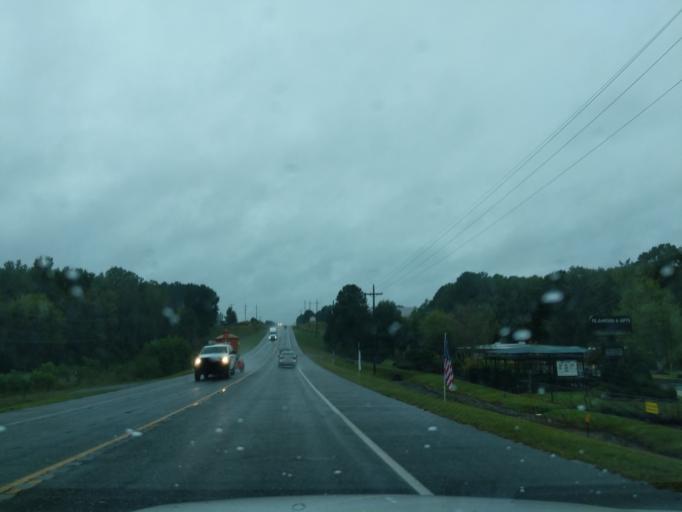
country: US
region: Louisiana
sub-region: Webster Parish
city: Minden
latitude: 32.6138
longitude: -93.2495
